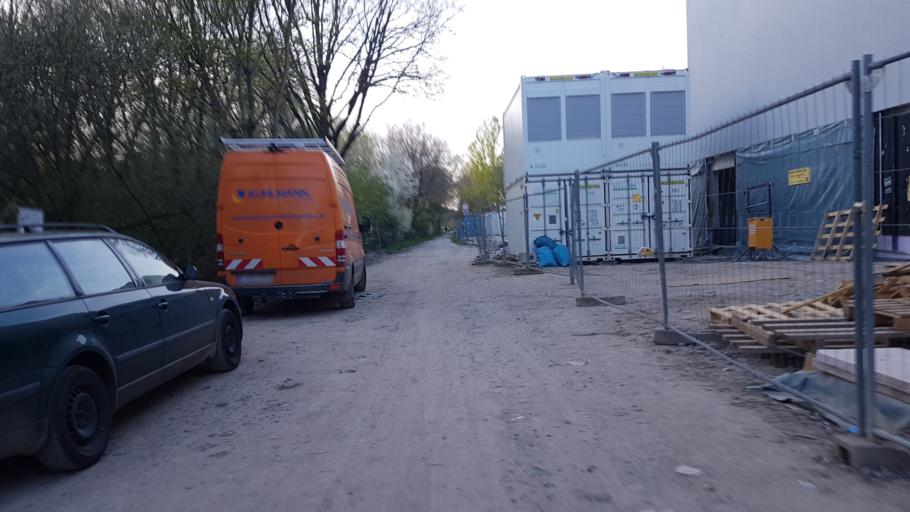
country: DE
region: Lower Saxony
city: Isernhagen Farster Bauerschaft
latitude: 52.4399
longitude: 9.8539
